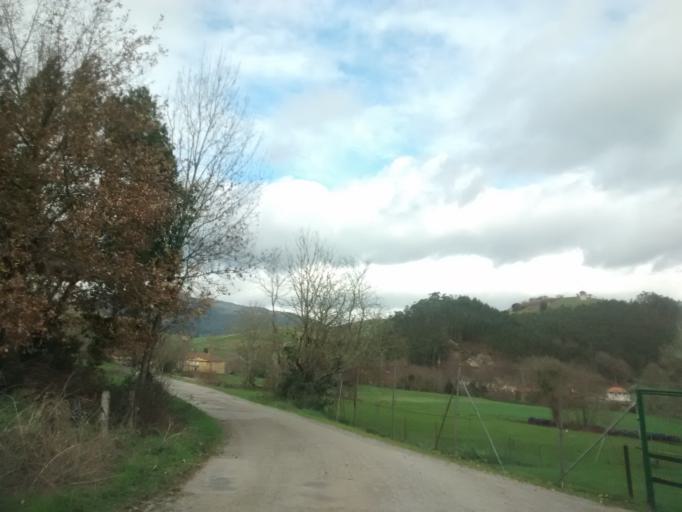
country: ES
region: Cantabria
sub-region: Provincia de Cantabria
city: Lierganes
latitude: 43.3426
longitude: -3.7374
